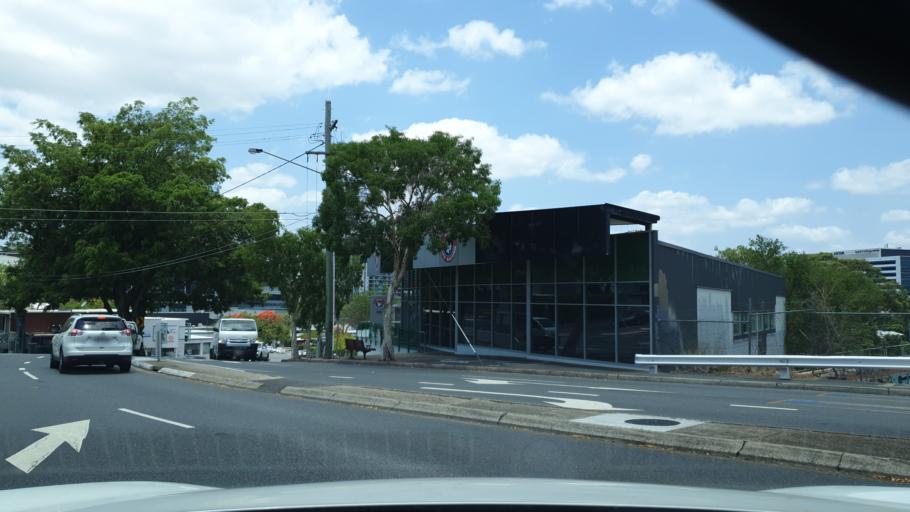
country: AU
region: Queensland
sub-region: Brisbane
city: Fortitude Valley
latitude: -27.4476
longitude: 153.0379
